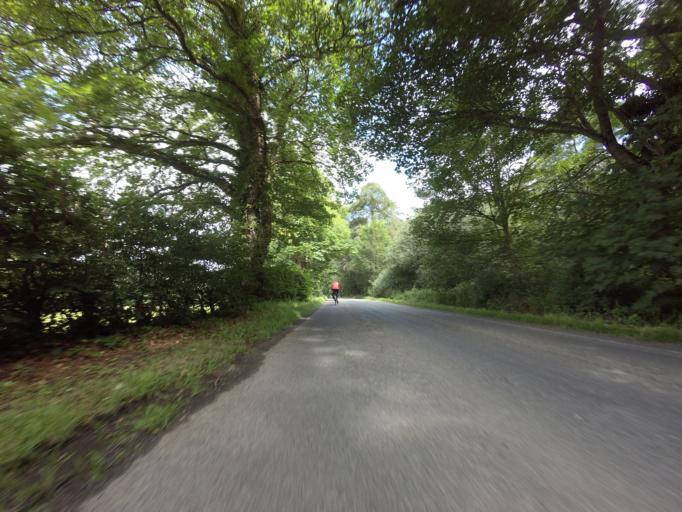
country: GB
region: Scotland
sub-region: Aberdeenshire
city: Turriff
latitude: 57.5515
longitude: -2.4870
